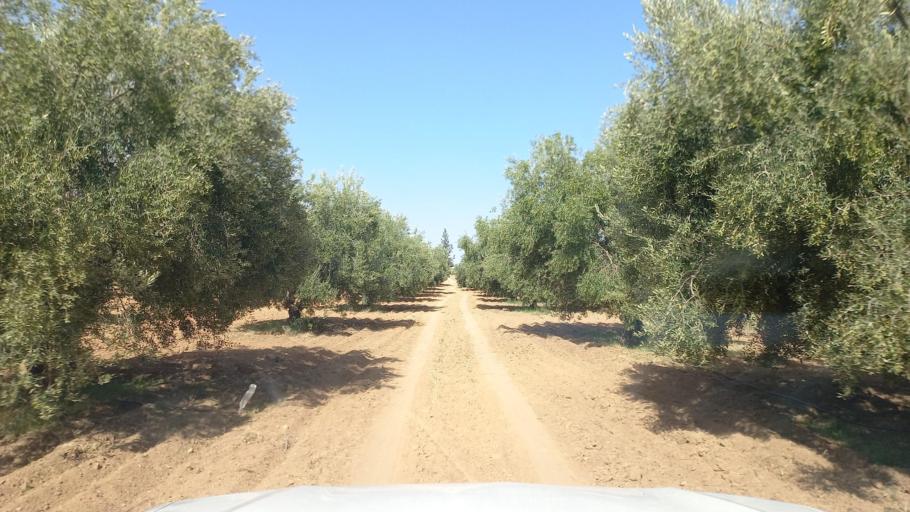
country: TN
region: Al Qasrayn
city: Kasserine
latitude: 35.2707
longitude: 9.0245
